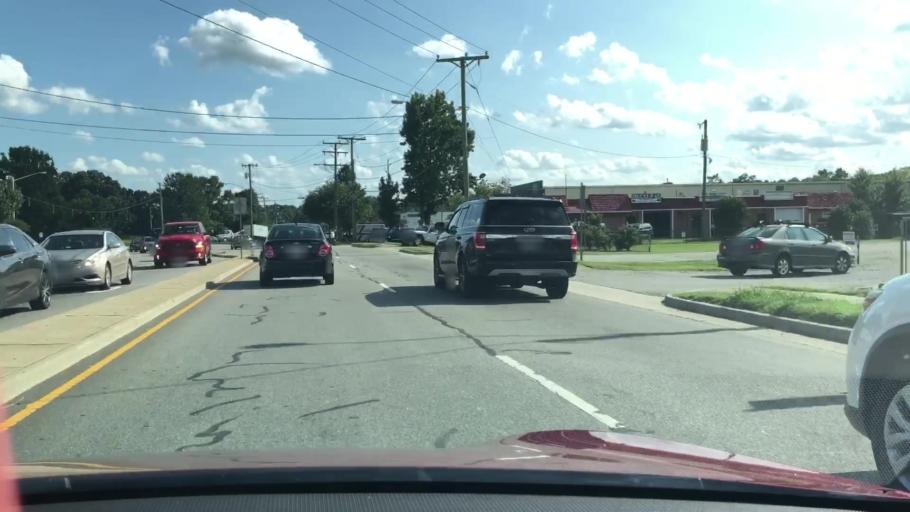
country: US
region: Virginia
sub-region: City of Virginia Beach
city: Virginia Beach
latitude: 36.8417
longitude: -76.0213
